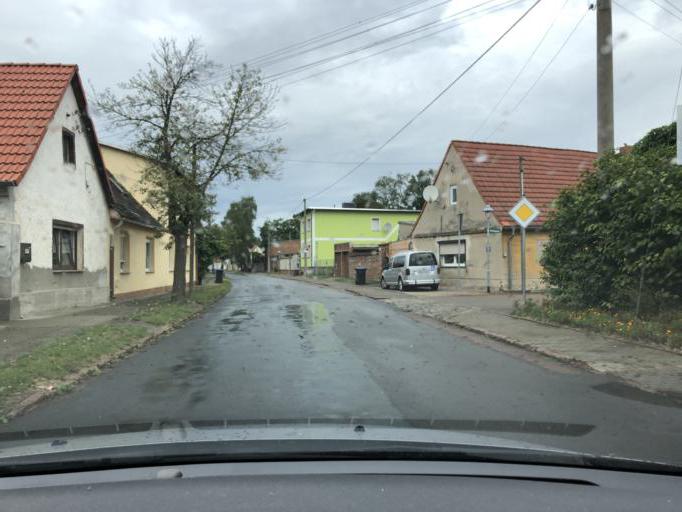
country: DE
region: Saxony-Anhalt
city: Wulfen
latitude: 51.8395
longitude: 11.8819
